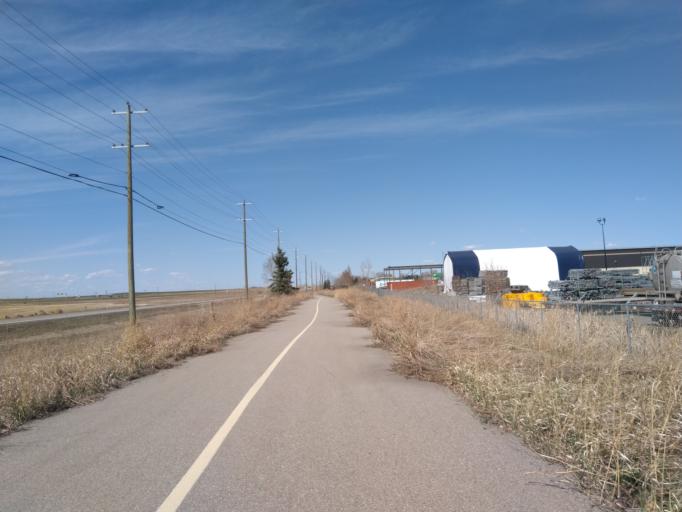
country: CA
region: Alberta
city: Chestermere
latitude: 50.9661
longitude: -113.9114
